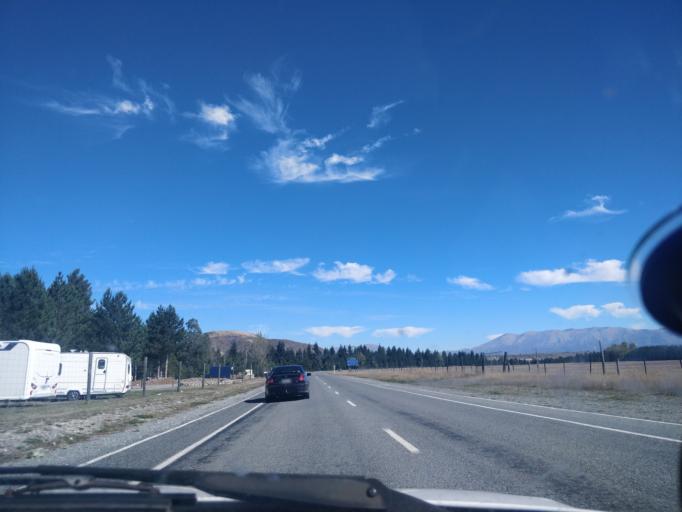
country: NZ
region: Otago
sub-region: Queenstown-Lakes District
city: Wanaka
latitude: -44.2702
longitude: 170.0635
